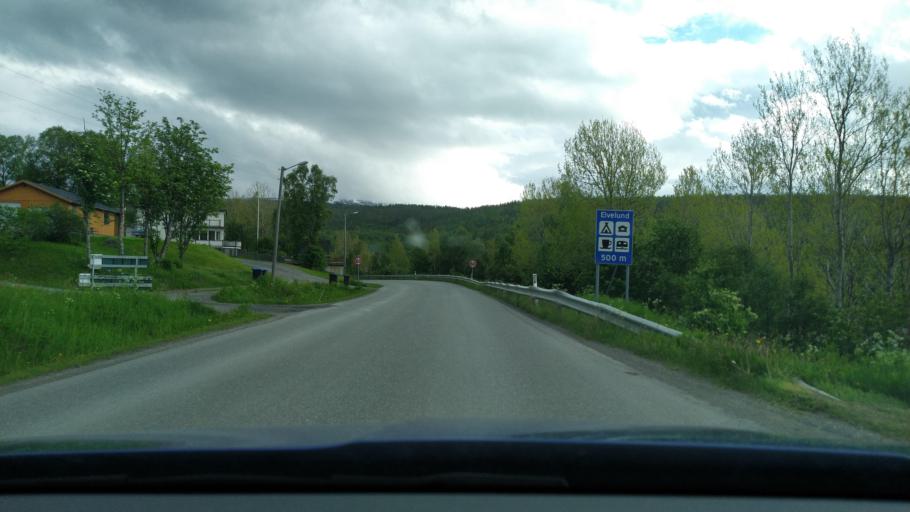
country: NO
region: Troms
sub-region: Salangen
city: Sjovegan
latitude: 68.8686
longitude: 17.8528
